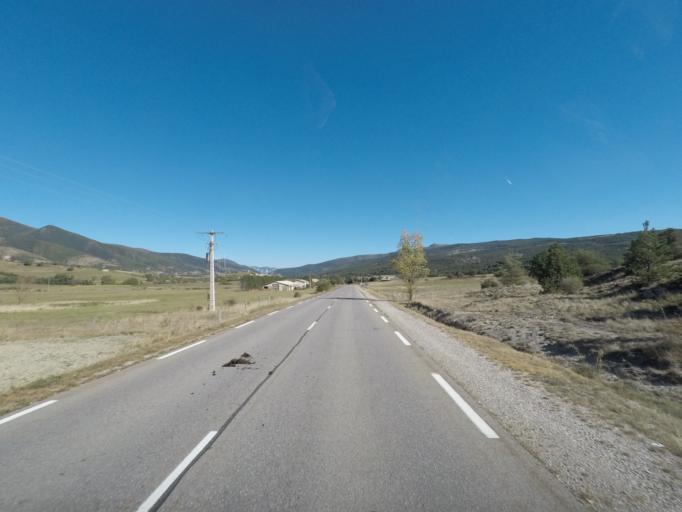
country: FR
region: Provence-Alpes-Cote d'Azur
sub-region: Departement des Hautes-Alpes
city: Serres
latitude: 44.4170
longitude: 5.5992
